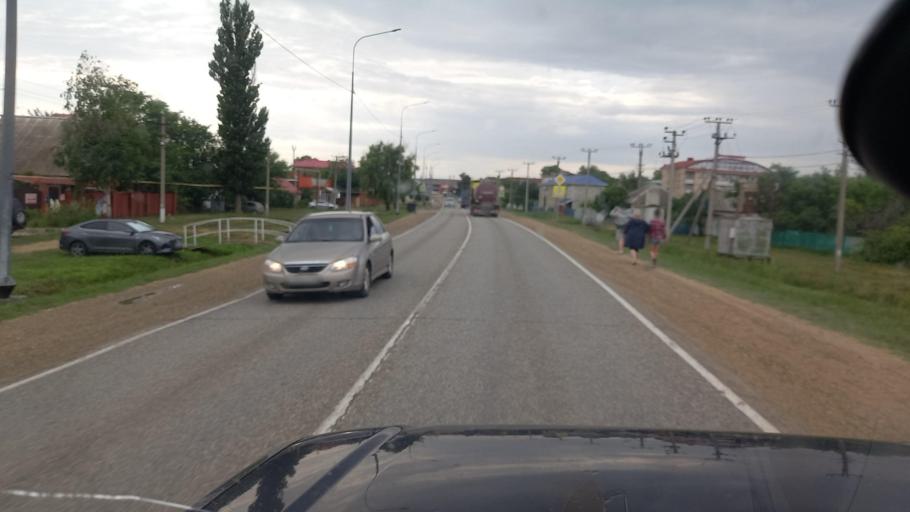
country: RU
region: Krasnodarskiy
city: Akhtanizovskaya
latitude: 45.3475
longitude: 37.1372
